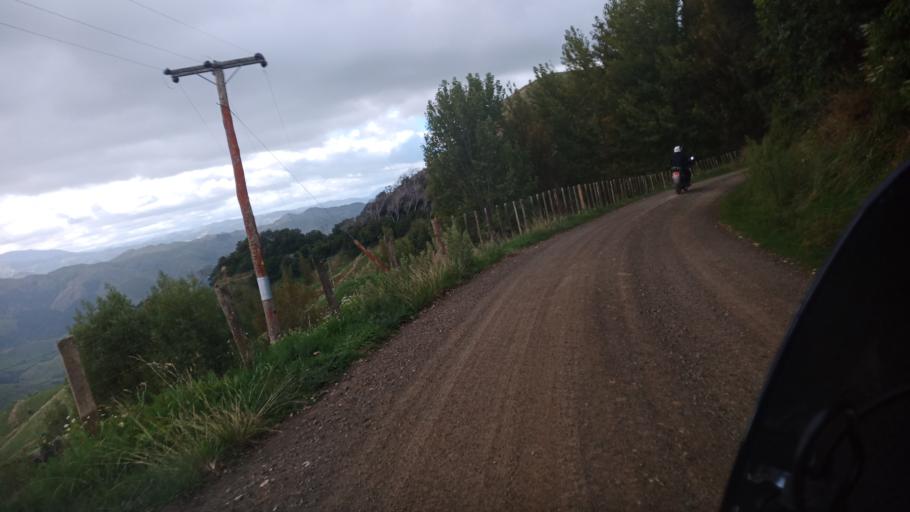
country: NZ
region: Gisborne
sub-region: Gisborne District
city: Gisborne
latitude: -38.4761
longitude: 177.6132
